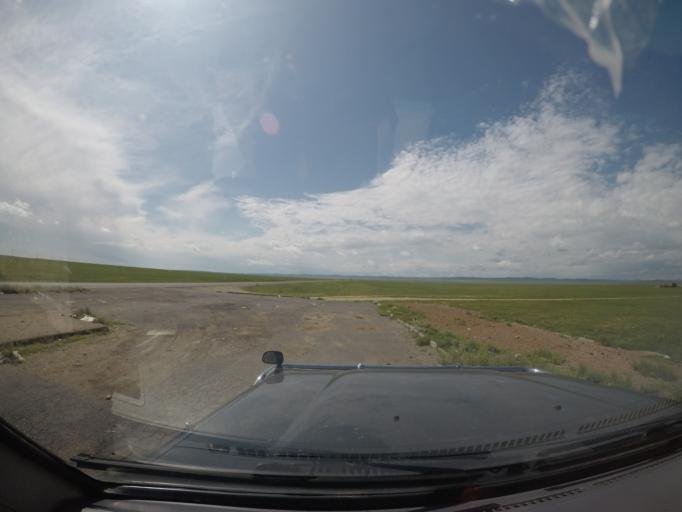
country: MN
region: Hentiy
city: Moron
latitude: 47.4217
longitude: 110.0804
